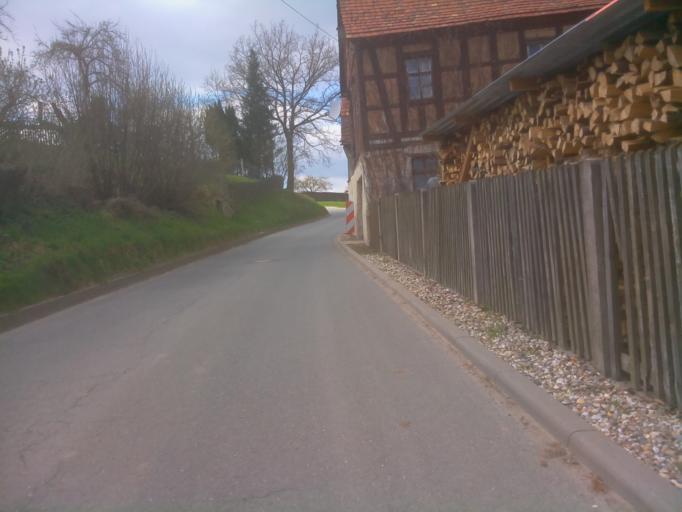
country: DE
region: Thuringia
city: Gneus
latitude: 50.8339
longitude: 11.6883
